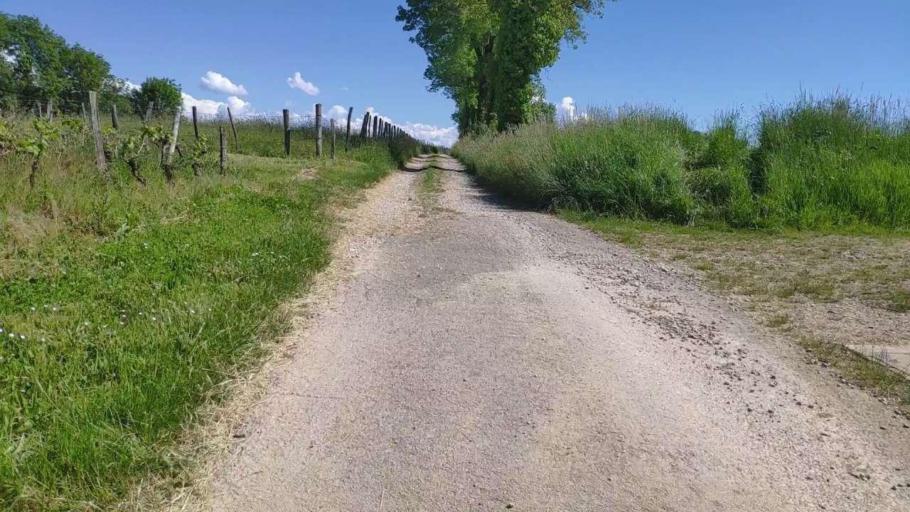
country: FR
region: Franche-Comte
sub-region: Departement du Jura
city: Perrigny
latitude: 46.7246
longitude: 5.5838
